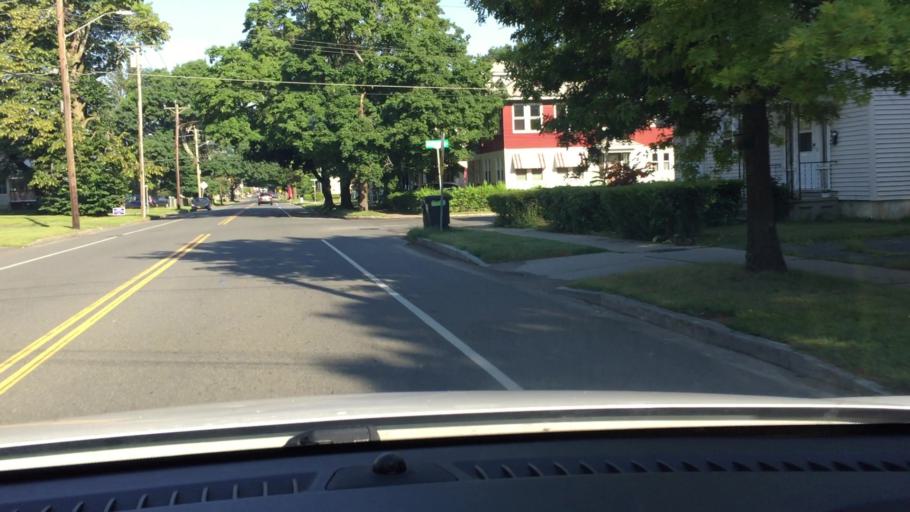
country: US
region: Massachusetts
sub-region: Berkshire County
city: Pittsfield
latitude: 42.4426
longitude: -73.2308
